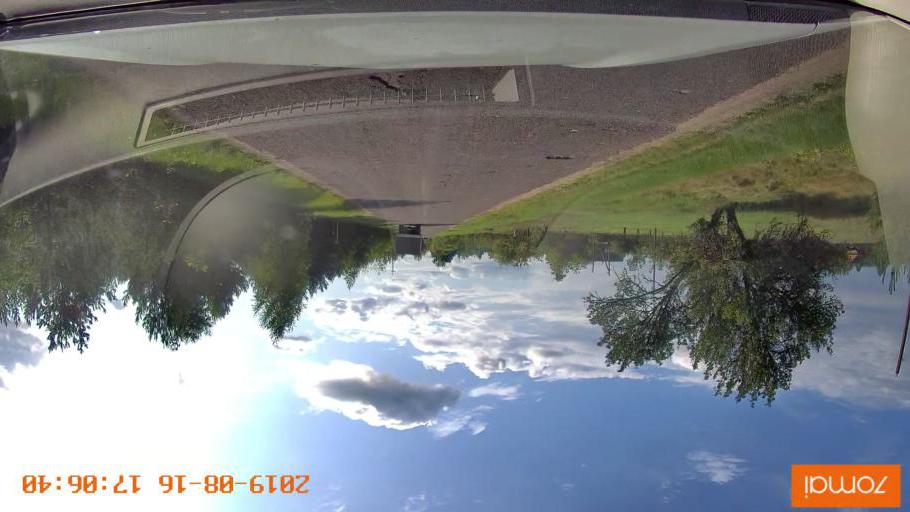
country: BY
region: Mogilev
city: Hlusha
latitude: 53.2242
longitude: 28.9303
